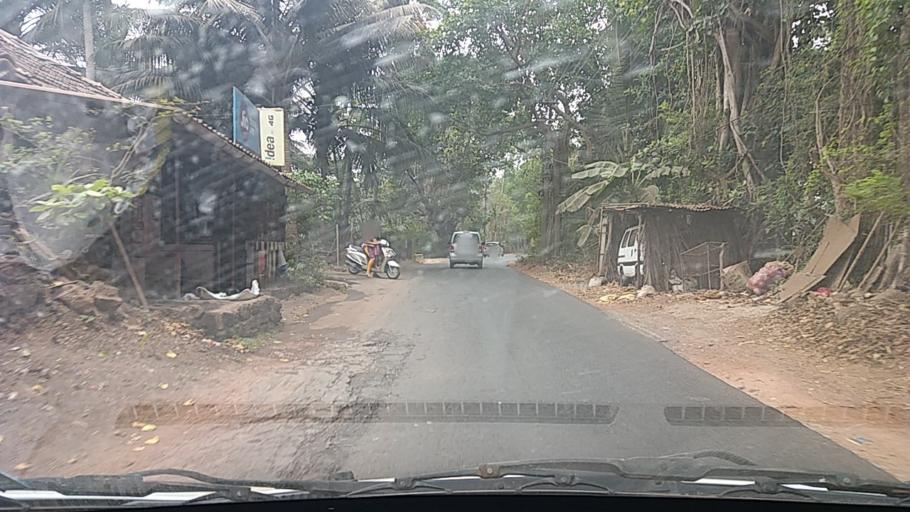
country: IN
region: Goa
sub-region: North Goa
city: Saligao
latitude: 15.5430
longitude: 73.7895
